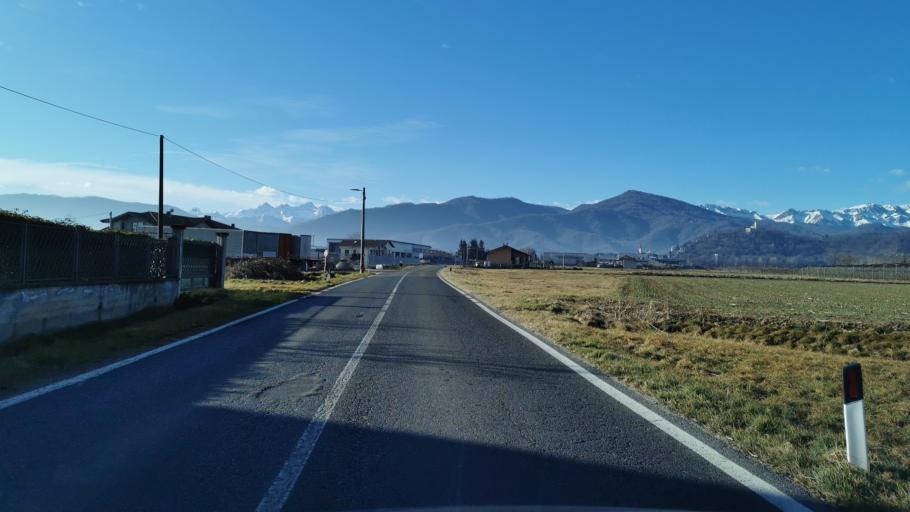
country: IT
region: Piedmont
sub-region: Provincia di Cuneo
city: Caraglio
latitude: 44.4293
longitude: 7.4467
